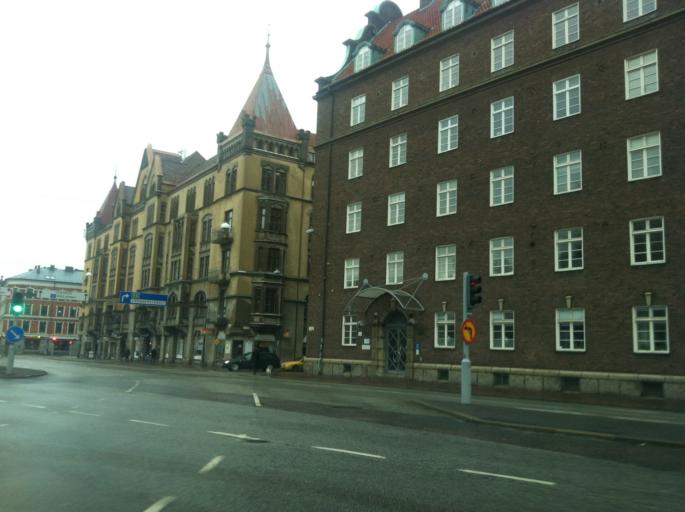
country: SE
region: Skane
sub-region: Malmo
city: Malmoe
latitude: 55.5981
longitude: 13.0097
